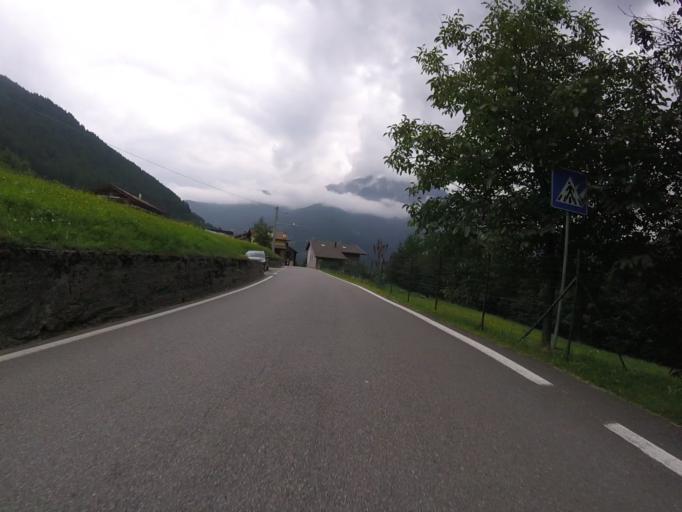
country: IT
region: Lombardy
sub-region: Provincia di Brescia
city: Monno
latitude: 46.2132
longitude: 10.3337
